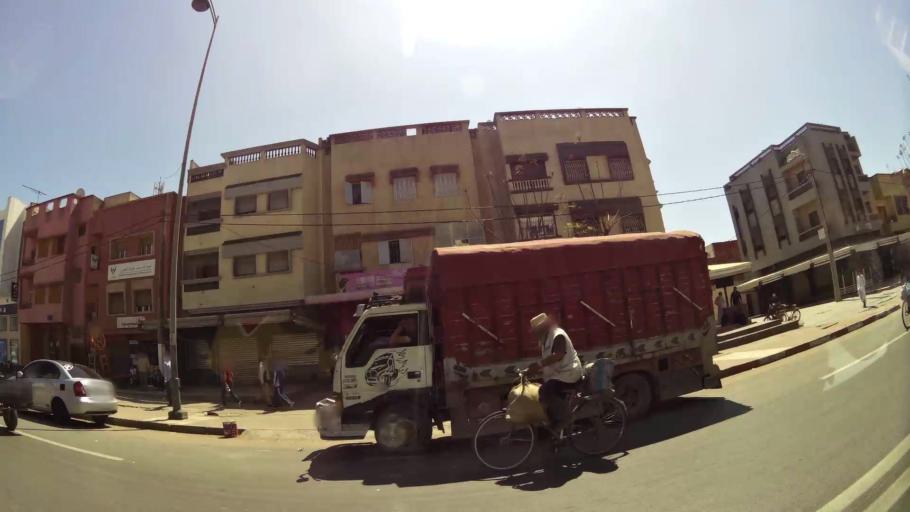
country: MA
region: Gharb-Chrarda-Beni Hssen
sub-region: Kenitra Province
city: Kenitra
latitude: 34.2428
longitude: -6.5498
